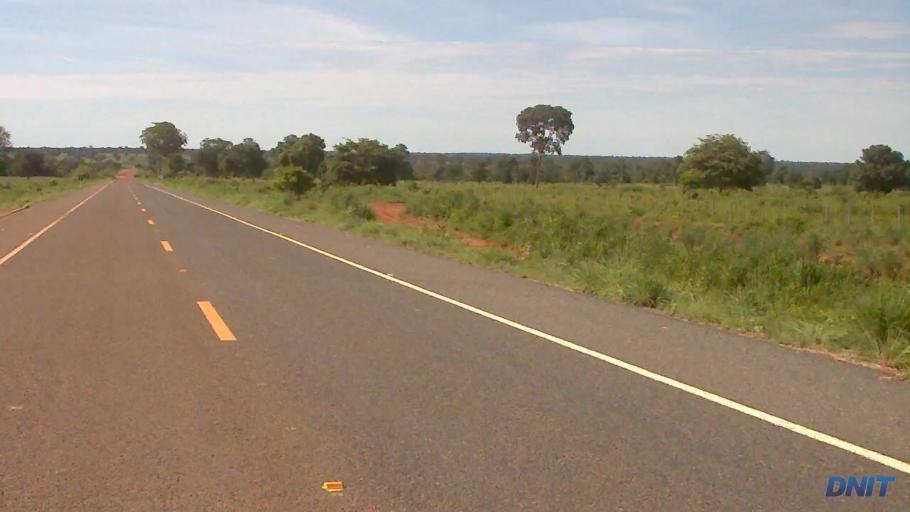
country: BR
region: Goias
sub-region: Sao Miguel Do Araguaia
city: Sao Miguel do Araguaia
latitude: -13.4926
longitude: -50.1085
